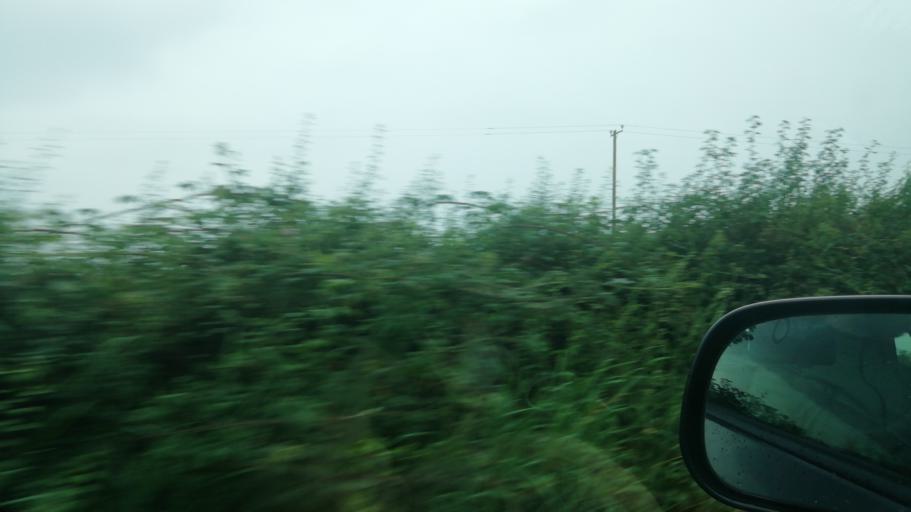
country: IE
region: Leinster
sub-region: Kilkenny
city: Thomastown
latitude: 52.6075
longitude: -7.1225
